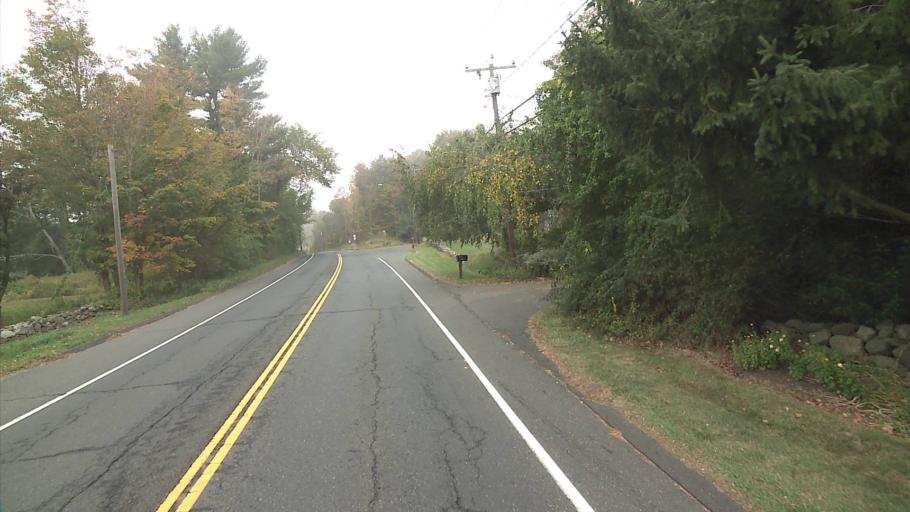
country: US
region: Connecticut
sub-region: Fairfield County
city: Newtown
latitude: 41.4182
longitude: -73.3303
